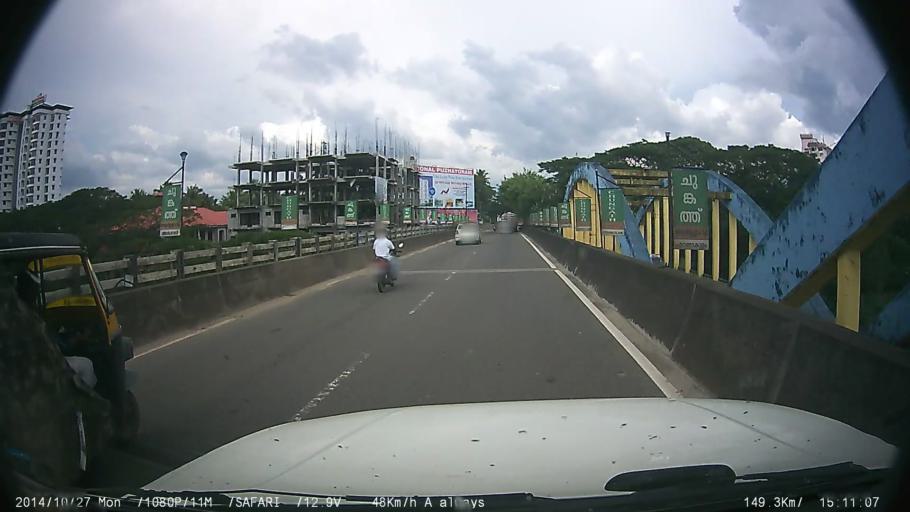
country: IN
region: Kerala
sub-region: Ernakulam
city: Aluva
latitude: 10.1261
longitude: 76.3410
